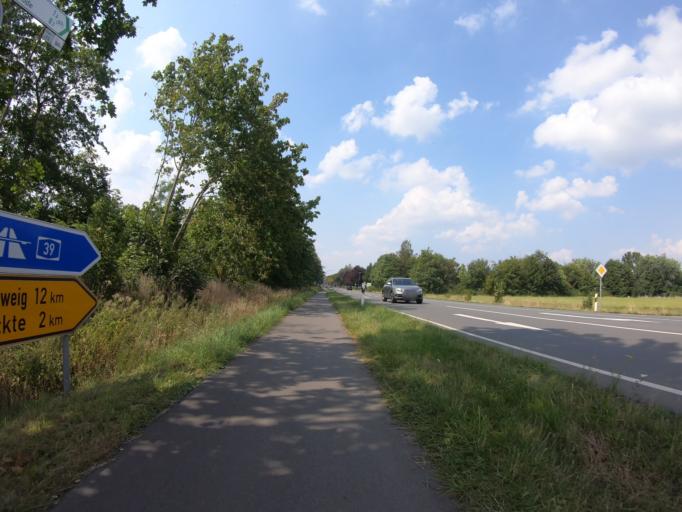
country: DE
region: Lower Saxony
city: Sickte
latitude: 52.2105
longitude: 10.6621
